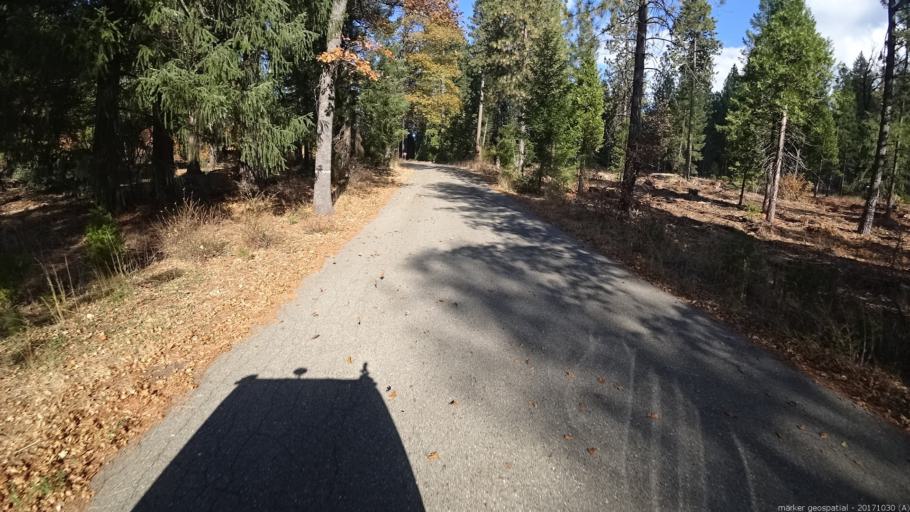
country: US
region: California
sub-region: Shasta County
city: Shingletown
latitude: 40.5164
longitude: -121.7303
